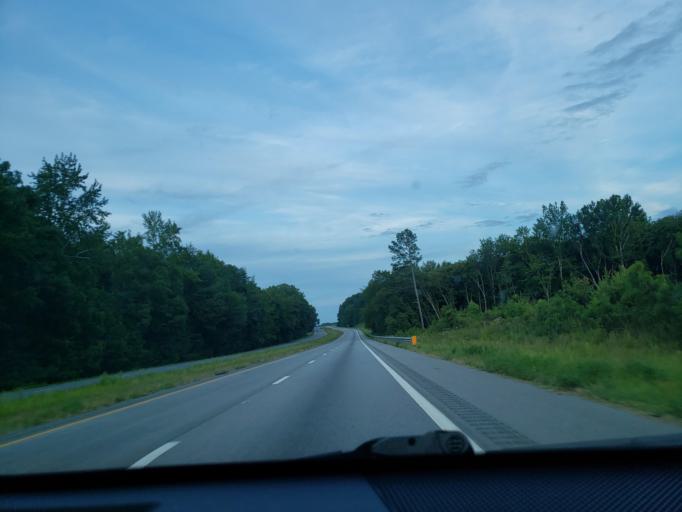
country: US
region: Virginia
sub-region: Southampton County
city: Courtland
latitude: 36.7039
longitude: -77.2759
